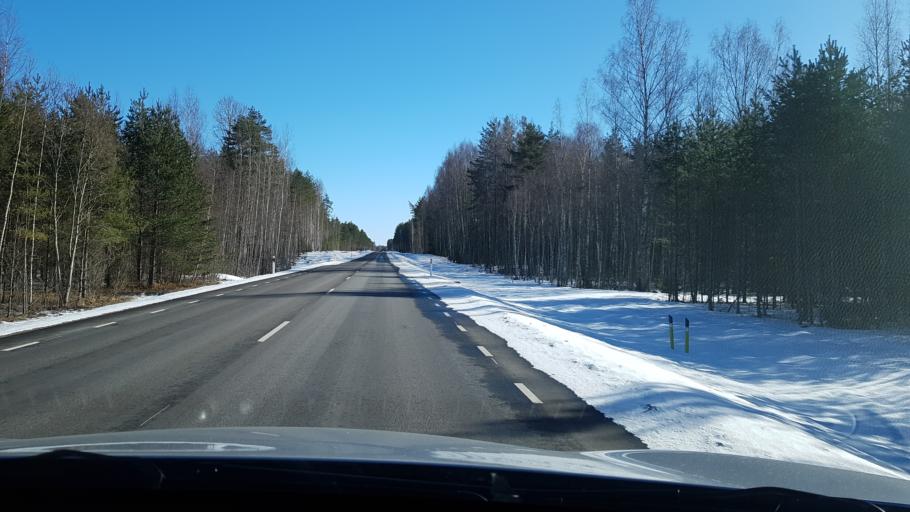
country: RU
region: Pskov
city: Pechory
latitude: 57.9689
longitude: 27.5930
